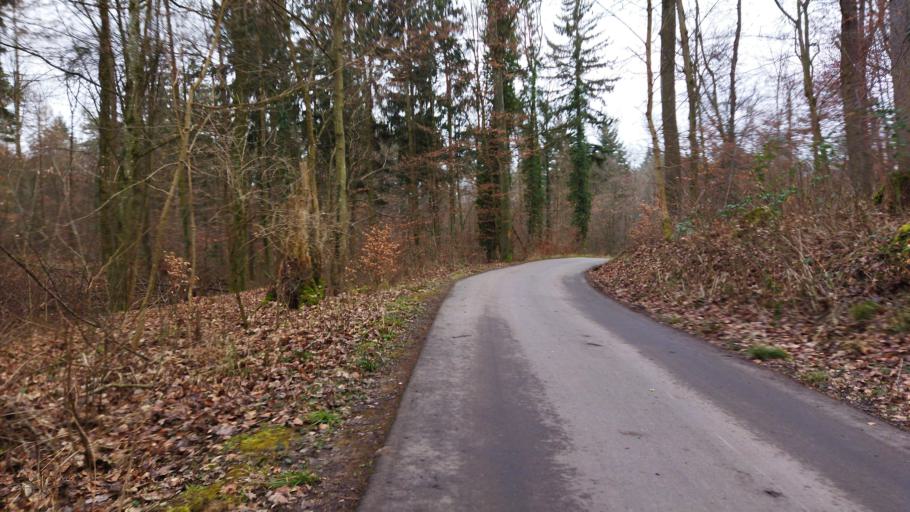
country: DE
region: Baden-Wuerttemberg
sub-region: Regierungsbezirk Stuttgart
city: Heilbronn
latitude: 49.1189
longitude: 9.2455
